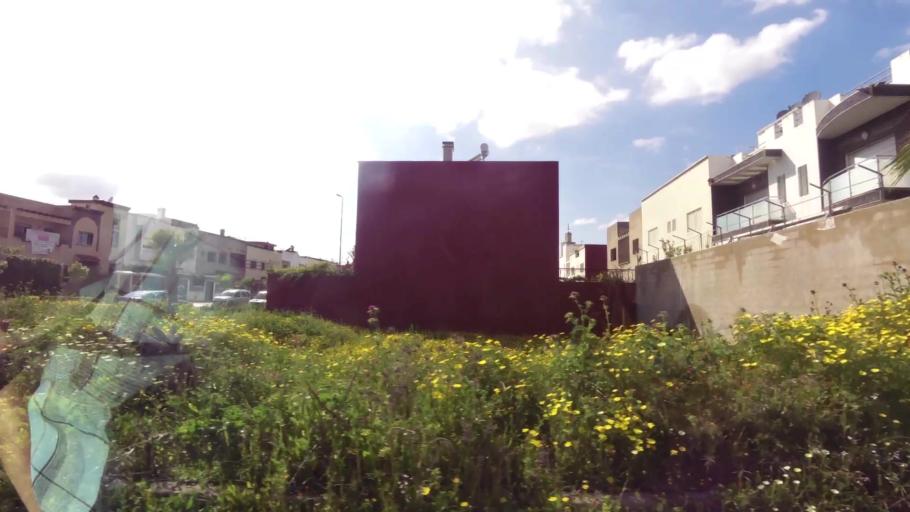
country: MA
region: Chaouia-Ouardigha
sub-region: Settat Province
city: Berrechid
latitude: 33.2575
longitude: -7.5645
